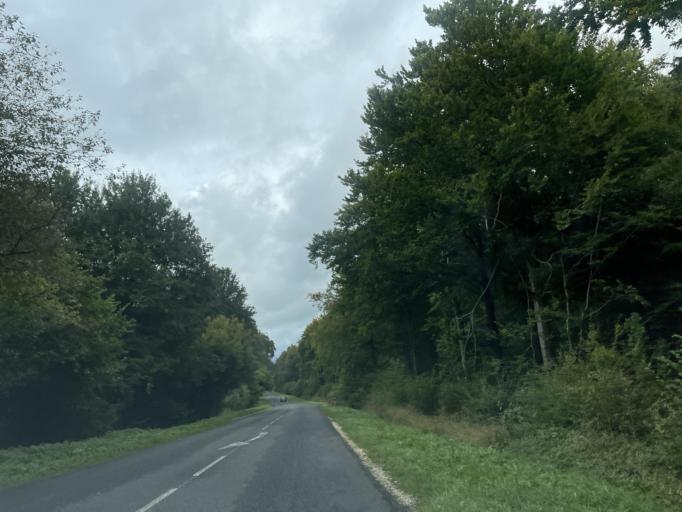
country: FR
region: Ile-de-France
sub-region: Departement de Seine-et-Marne
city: Saint-Jean-les-Deux-Jumeaux
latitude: 48.9170
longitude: 3.0117
